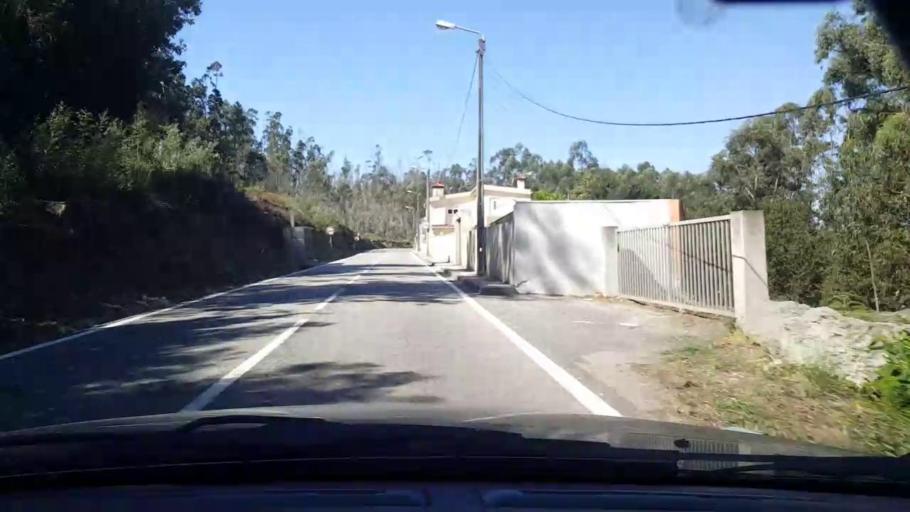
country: PT
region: Porto
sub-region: Vila do Conde
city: Arvore
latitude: 41.3417
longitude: -8.6541
